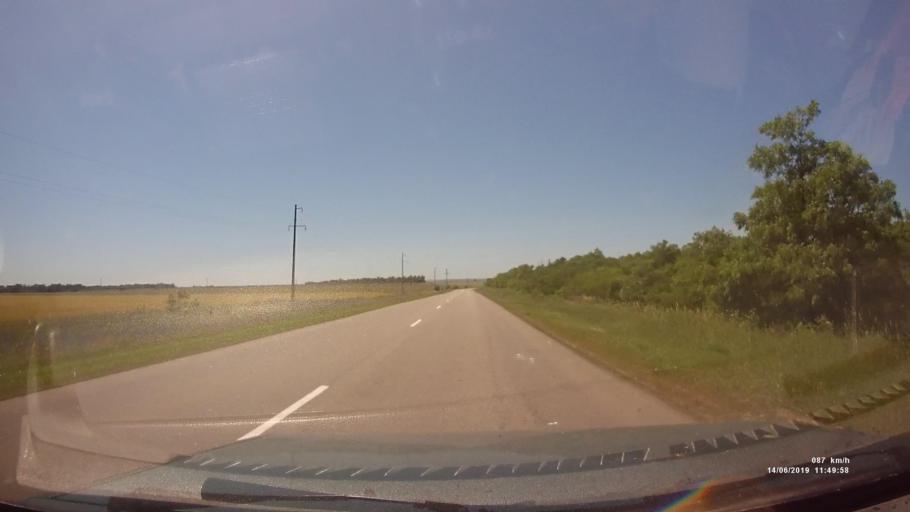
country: RU
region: Rostov
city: Kazanskaya
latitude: 49.8499
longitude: 41.2723
